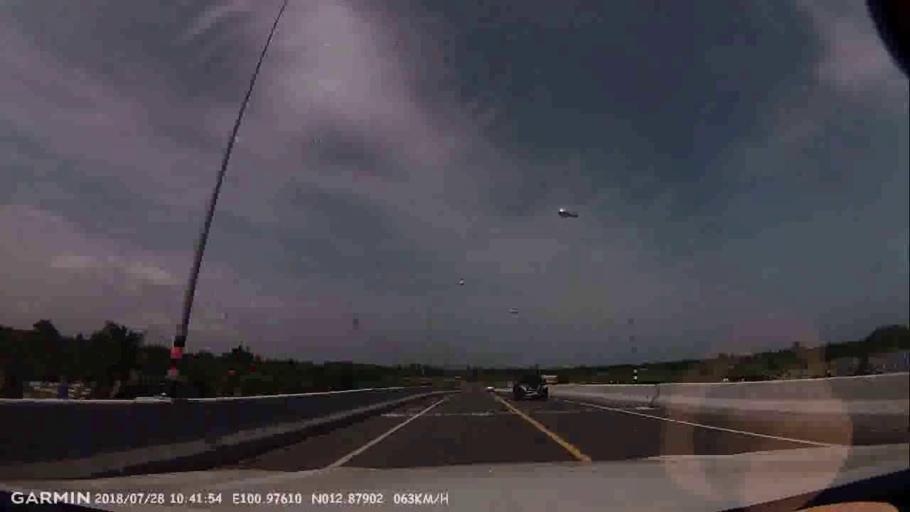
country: TH
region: Chon Buri
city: Phatthaya
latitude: 12.8777
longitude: 100.9759
